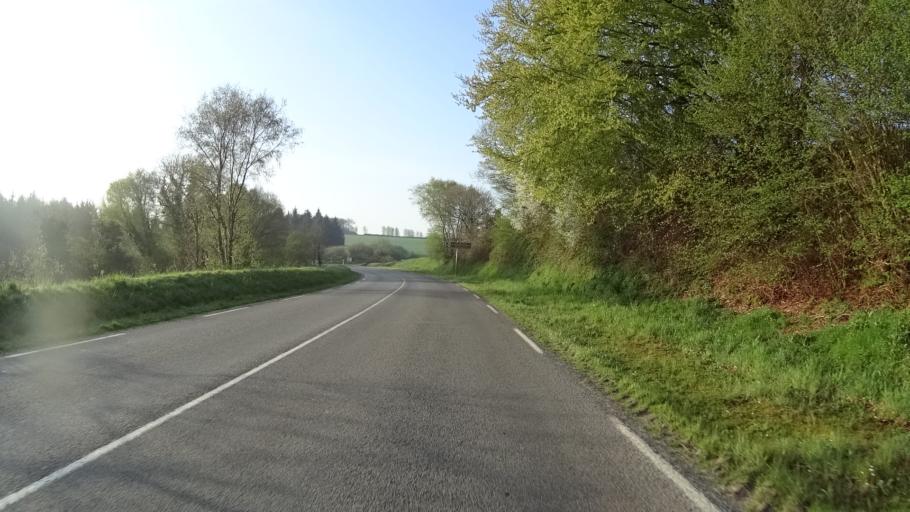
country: FR
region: Brittany
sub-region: Departement du Finistere
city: Sizun
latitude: 48.4167
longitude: -4.1005
